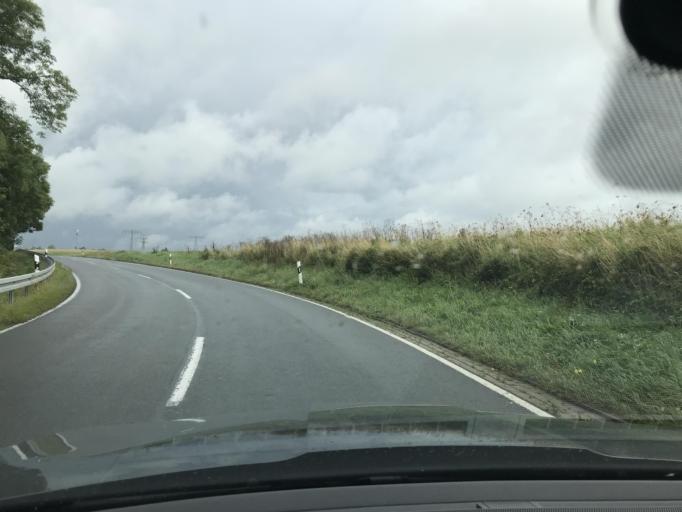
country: DE
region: Saxony-Anhalt
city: Huttenrode
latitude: 51.7648
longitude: 10.8881
